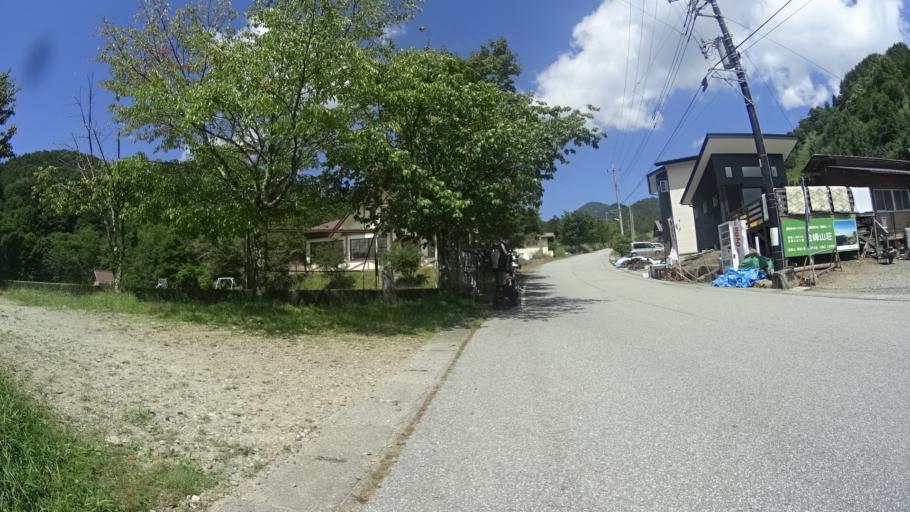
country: JP
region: Yamanashi
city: Enzan
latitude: 35.8101
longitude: 138.6551
